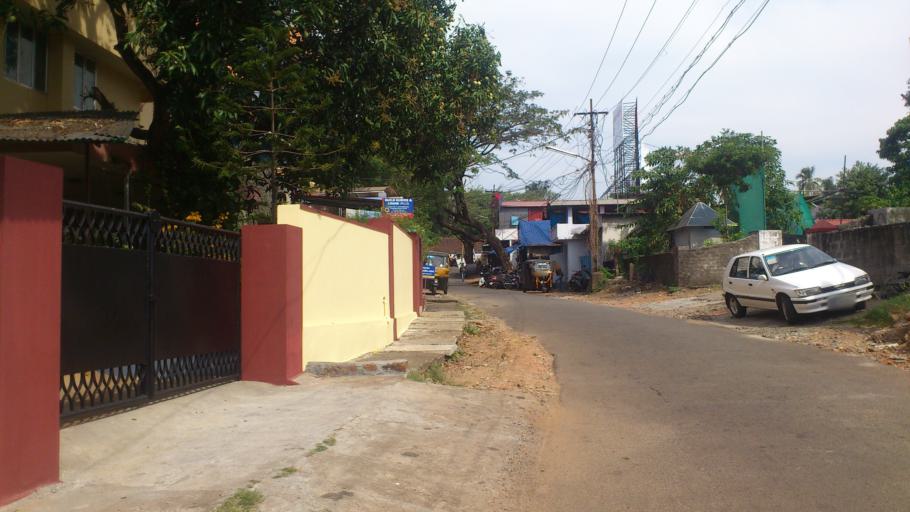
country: IN
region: Kerala
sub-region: Thrissur District
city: Trichur
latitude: 10.5226
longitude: 76.2086
